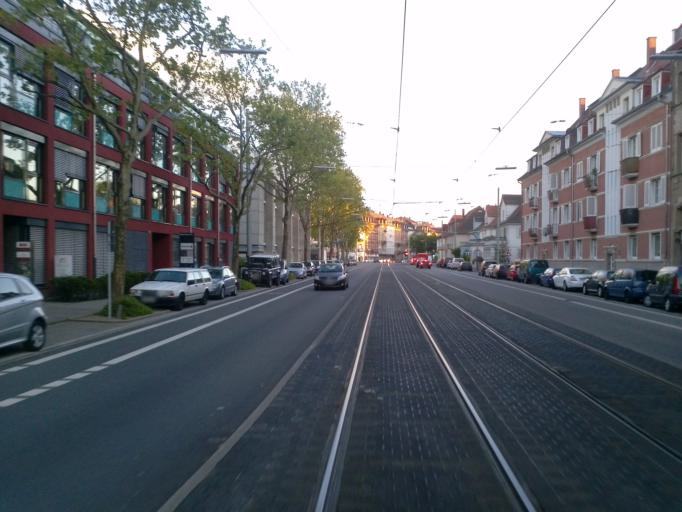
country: DE
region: Baden-Wuerttemberg
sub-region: Karlsruhe Region
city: Karlsruhe
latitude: 49.0128
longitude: 8.3750
